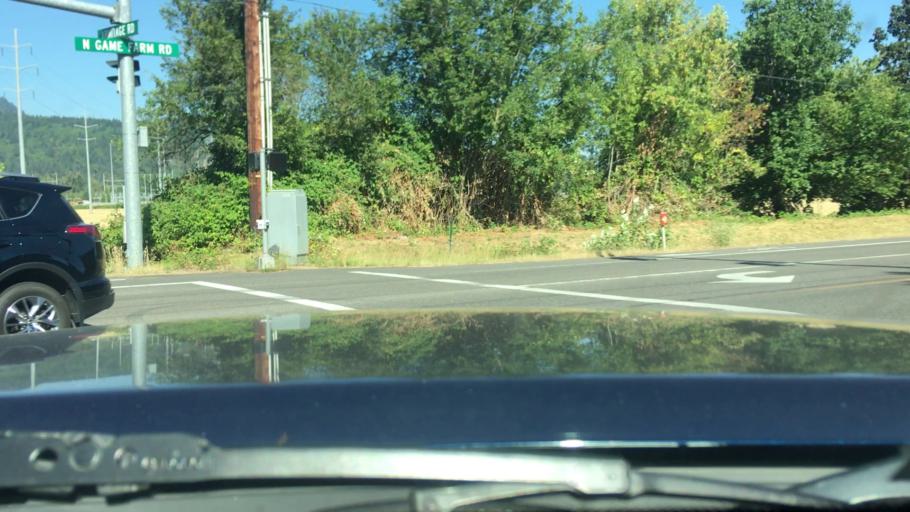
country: US
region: Oregon
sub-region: Lane County
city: Coburg
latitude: 44.0946
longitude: -123.0515
